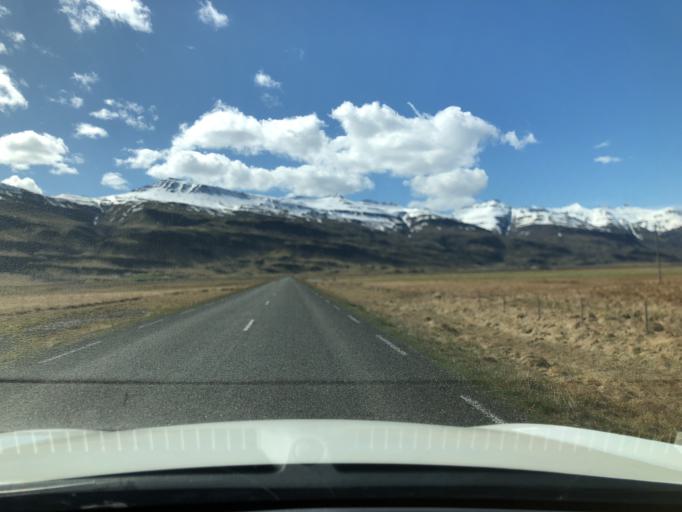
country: IS
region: East
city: Reydarfjoerdur
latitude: 64.5590
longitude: -14.6052
